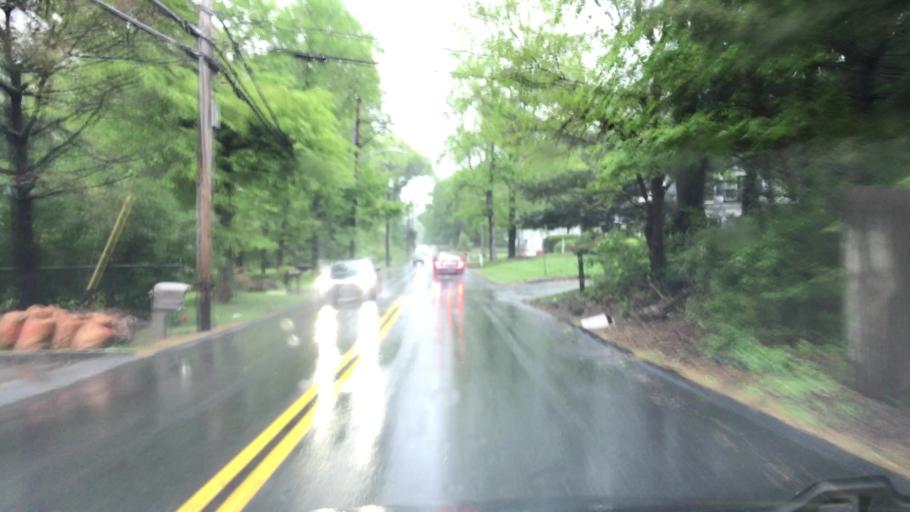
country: US
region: New York
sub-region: Rockland County
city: New Square
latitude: 41.1224
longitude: -74.0212
